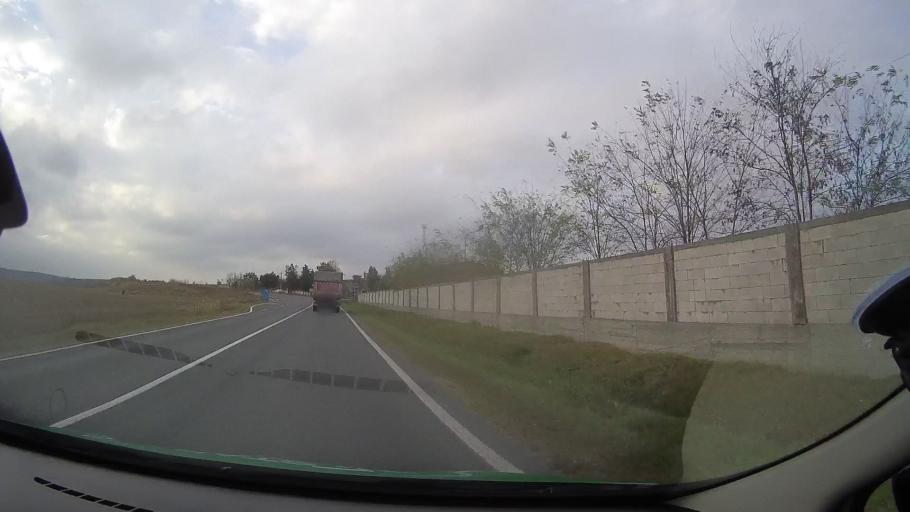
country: RO
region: Constanta
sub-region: Comuna Mircea Voda
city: Mircea Voda
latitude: 44.2706
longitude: 28.1737
